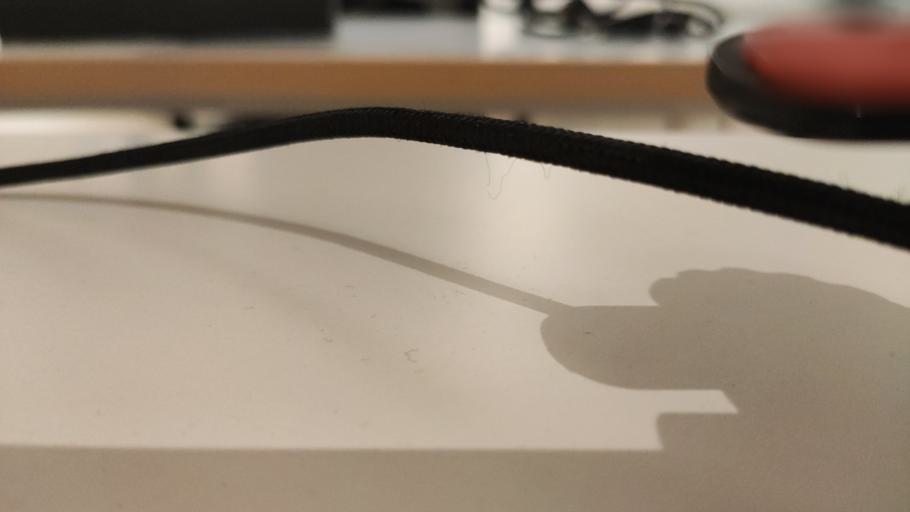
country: RU
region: Moskovskaya
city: Dorokhovo
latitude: 55.4537
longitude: 36.3528
